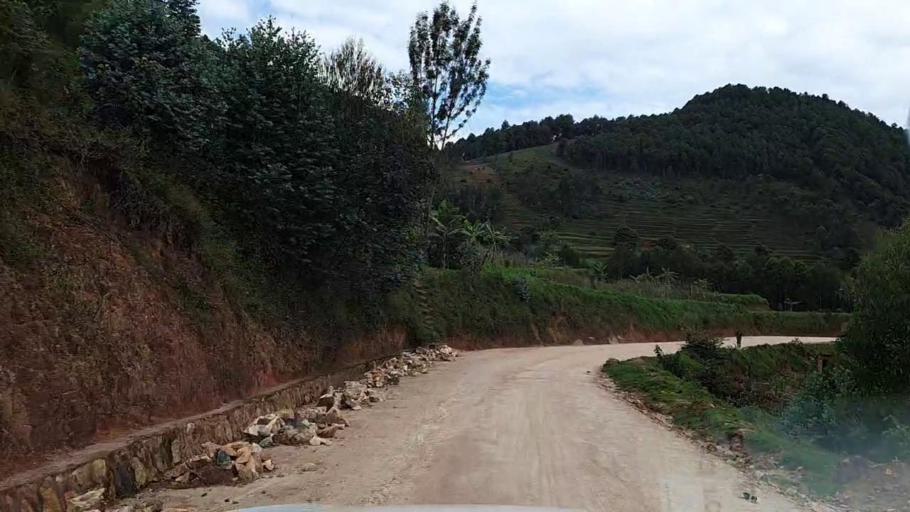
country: RW
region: Southern Province
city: Nzega
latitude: -2.4025
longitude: 29.4535
